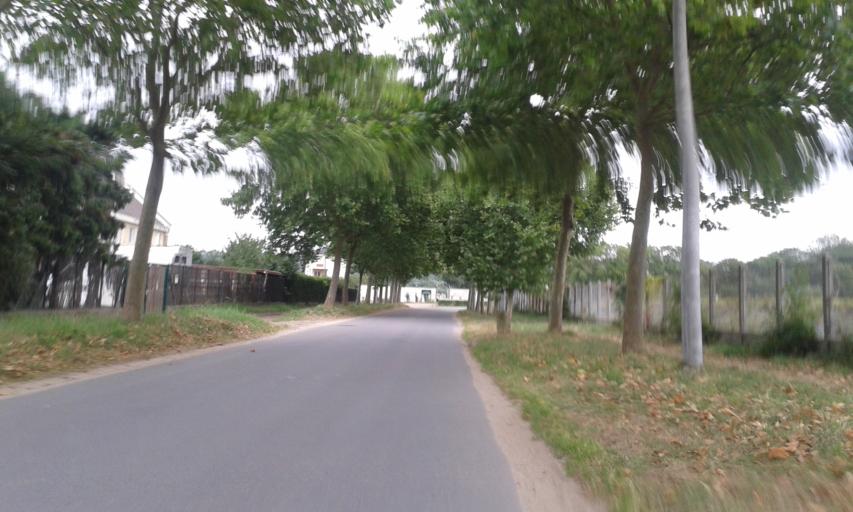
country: FR
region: Ile-de-France
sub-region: Departement du Val-d'Oise
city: La Frette-sur-Seine
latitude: 48.9629
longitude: 2.1726
